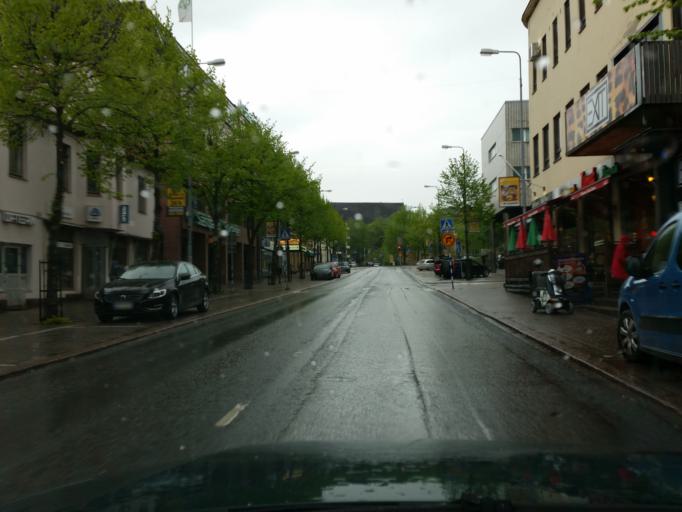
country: FI
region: Uusimaa
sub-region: Helsinki
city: Lohja
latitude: 60.2504
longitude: 24.0644
